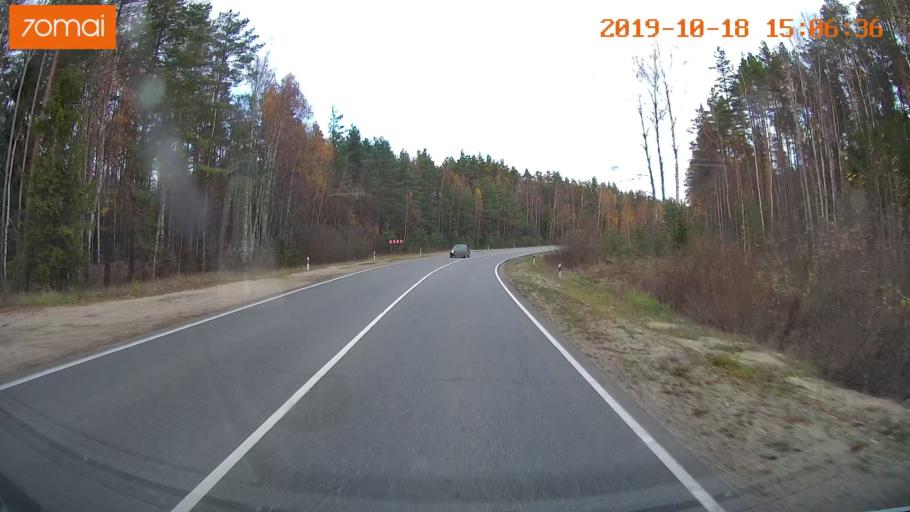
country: RU
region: Vladimir
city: Gus'-Khrustal'nyy
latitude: 55.5324
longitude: 40.5799
